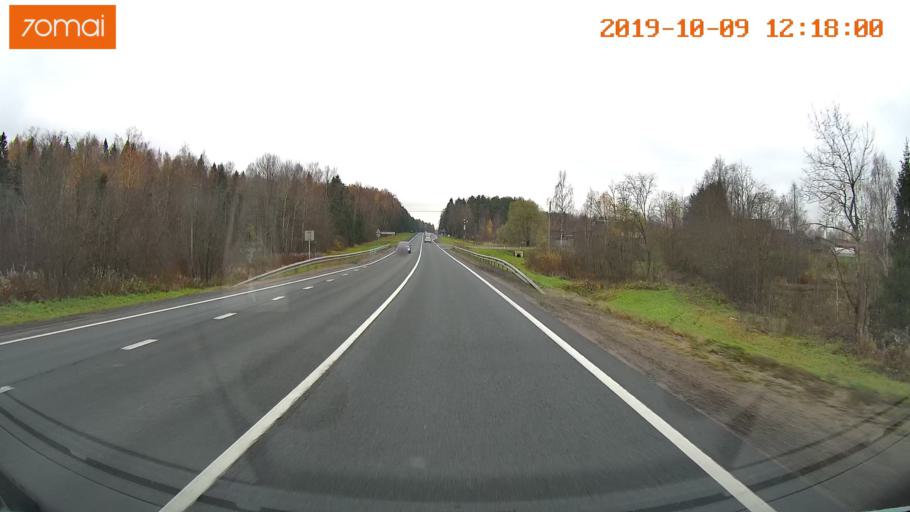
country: RU
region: Jaroslavl
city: Prechistoye
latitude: 58.4485
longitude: 40.3207
